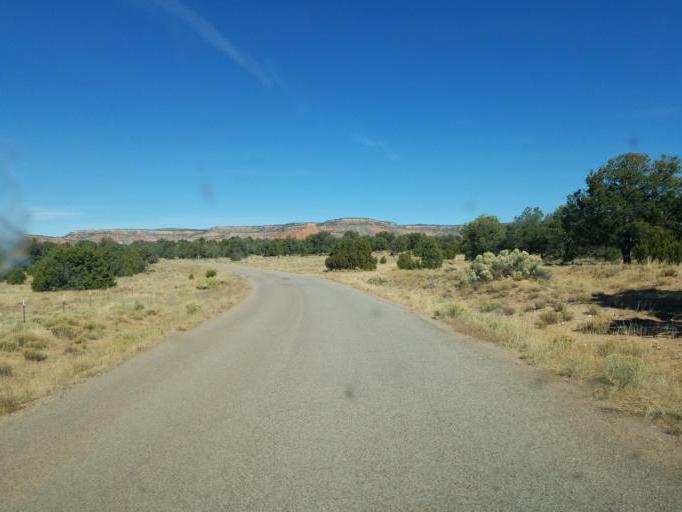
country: US
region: New Mexico
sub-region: McKinley County
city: Thoreau
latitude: 35.4221
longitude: -108.2834
